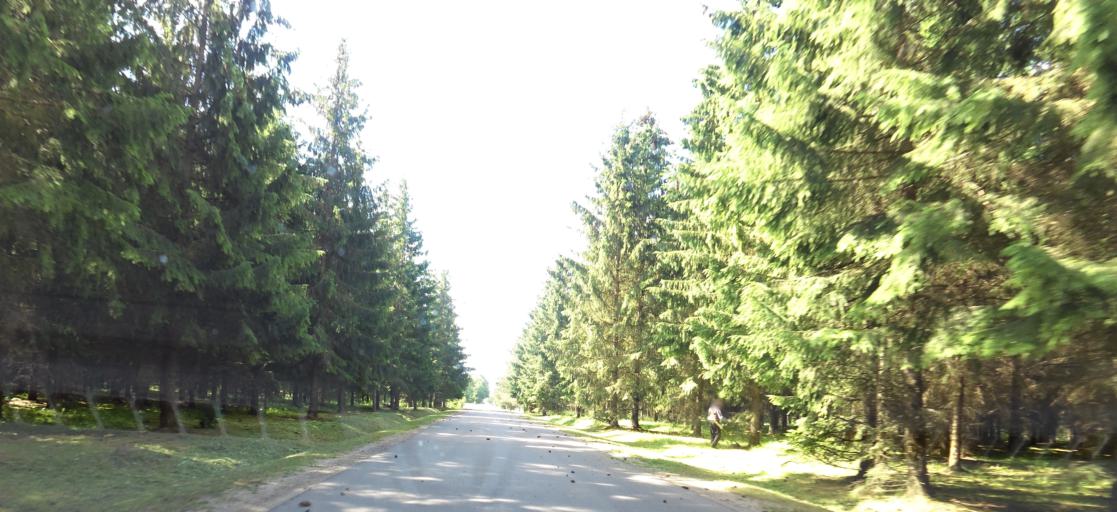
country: LT
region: Panevezys
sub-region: Birzai
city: Birzai
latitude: 56.1854
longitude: 24.7595
